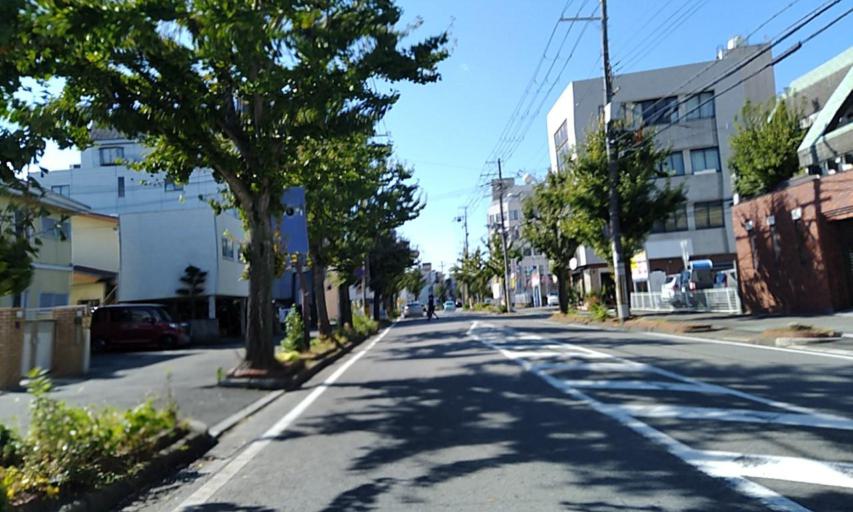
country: JP
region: Wakayama
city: Wakayama-shi
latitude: 34.2353
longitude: 135.1836
